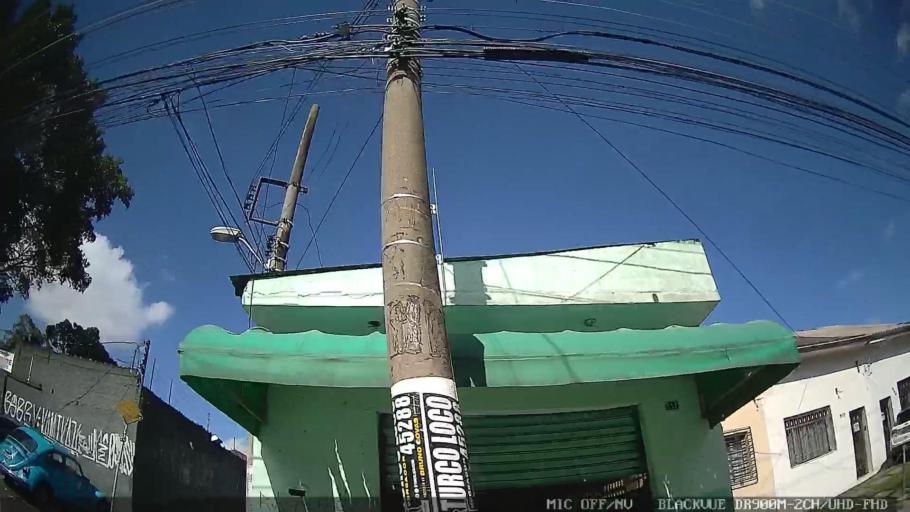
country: BR
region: Sao Paulo
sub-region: Sao Caetano Do Sul
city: Sao Caetano do Sul
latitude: -23.6065
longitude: -46.5985
